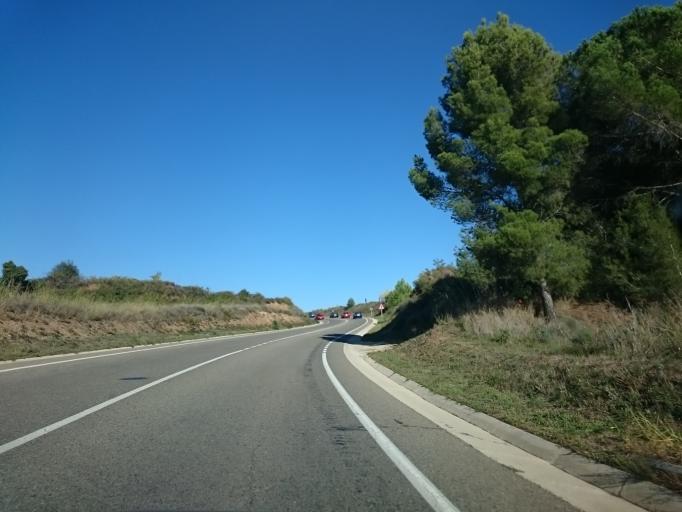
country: ES
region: Catalonia
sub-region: Provincia de Barcelona
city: Piera
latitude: 41.5327
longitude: 1.7266
